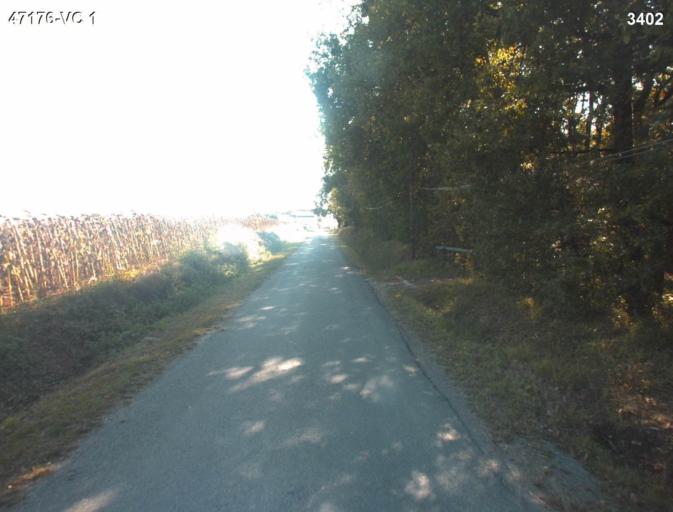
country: FR
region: Aquitaine
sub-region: Departement du Lot-et-Garonne
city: Vianne
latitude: 44.2203
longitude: 0.3051
